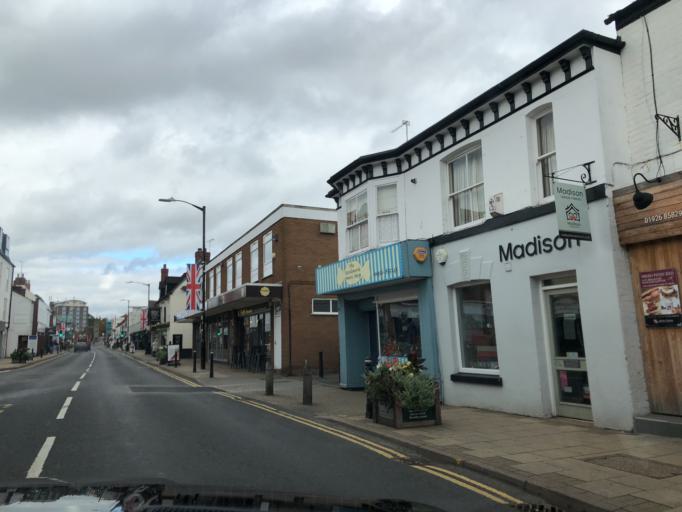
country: GB
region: England
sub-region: Warwickshire
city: Kenilworth
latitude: 52.3410
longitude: -1.5774
